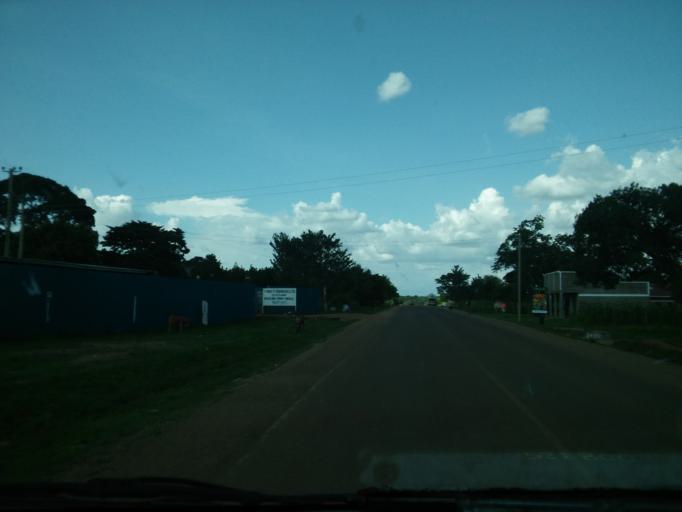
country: UG
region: Eastern Region
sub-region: Kibuku District
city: Kibuku
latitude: 1.0060
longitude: 33.7761
